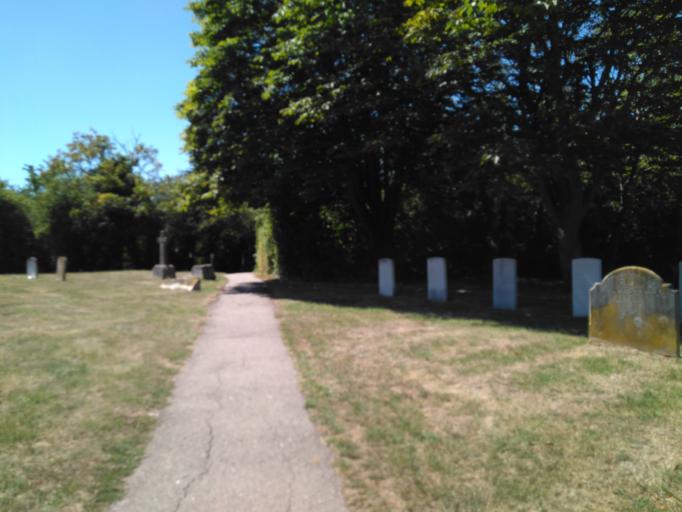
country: GB
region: England
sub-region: Kent
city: Tankerton
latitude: 51.3550
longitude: 1.0397
